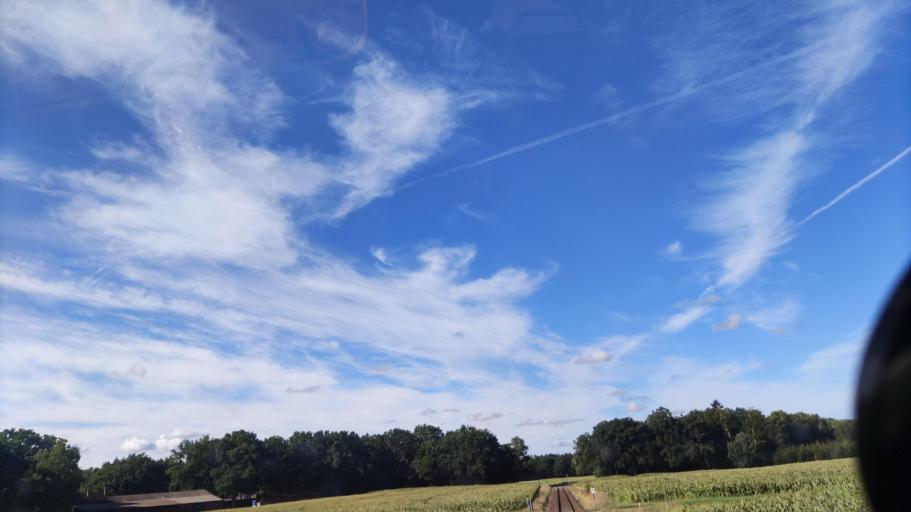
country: DE
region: Lower Saxony
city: Soltau
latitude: 53.0170
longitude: 9.8970
